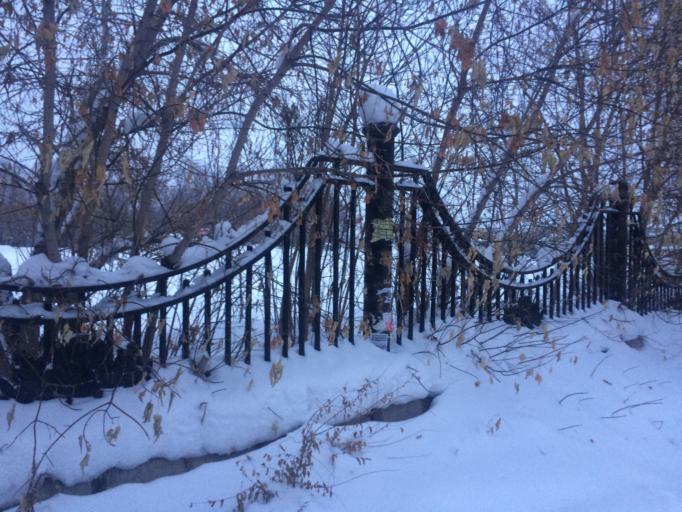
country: RU
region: Chelyabinsk
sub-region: Gorod Magnitogorsk
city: Magnitogorsk
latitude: 53.4016
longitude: 58.9859
